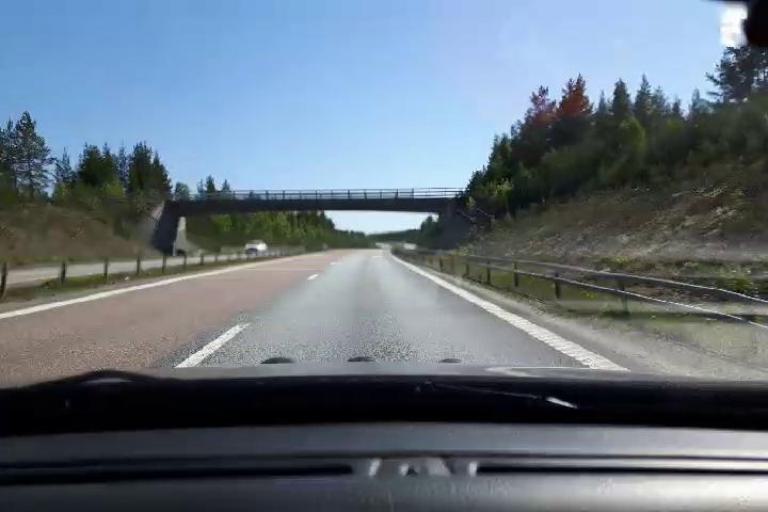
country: SE
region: Gaevleborg
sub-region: Soderhamns Kommun
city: Soderhamn
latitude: 61.4691
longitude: 16.9899
